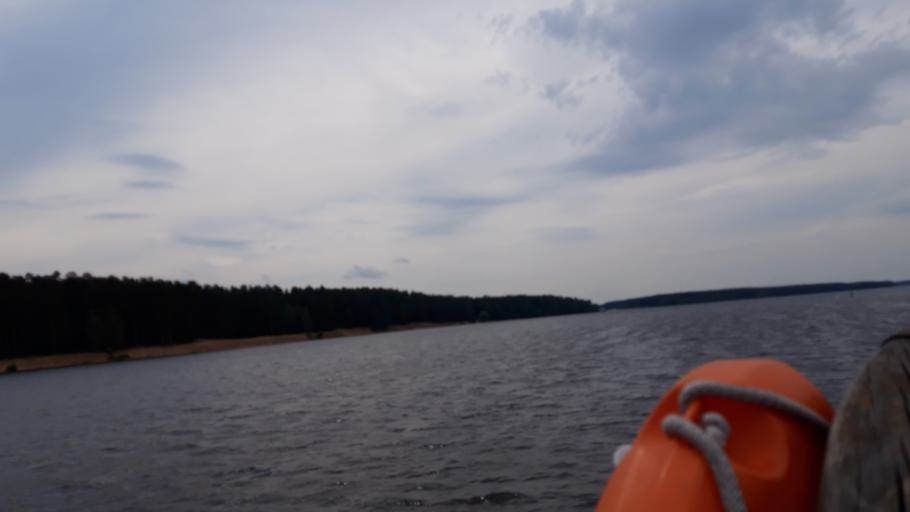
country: RU
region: Tverskaya
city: Konakovo
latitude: 56.7089
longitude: 36.7507
